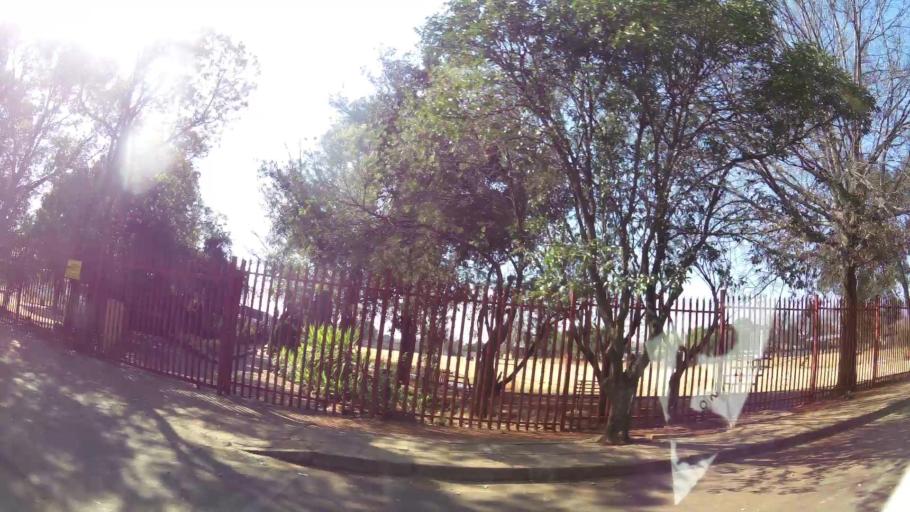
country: ZA
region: Gauteng
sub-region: Ekurhuleni Metropolitan Municipality
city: Boksburg
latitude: -26.2440
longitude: 28.2641
